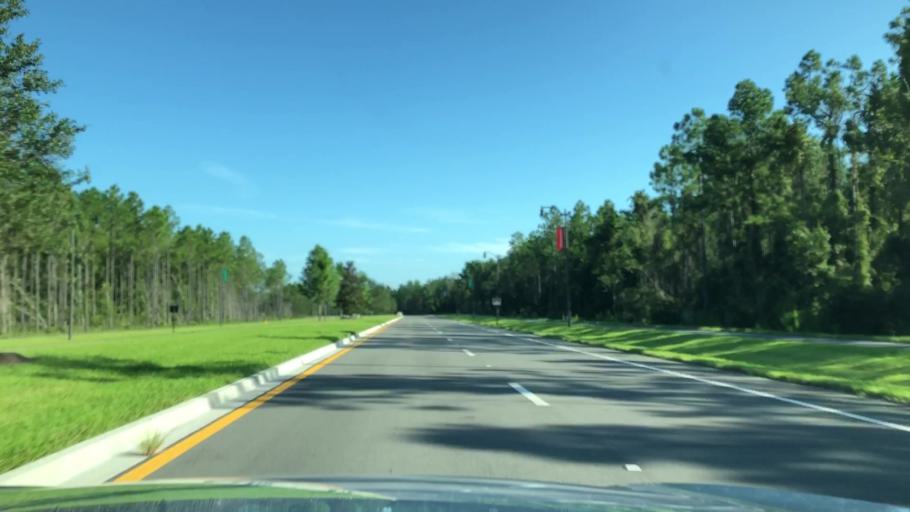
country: US
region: Florida
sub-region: Saint Johns County
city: Palm Valley
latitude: 30.0769
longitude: -81.4015
